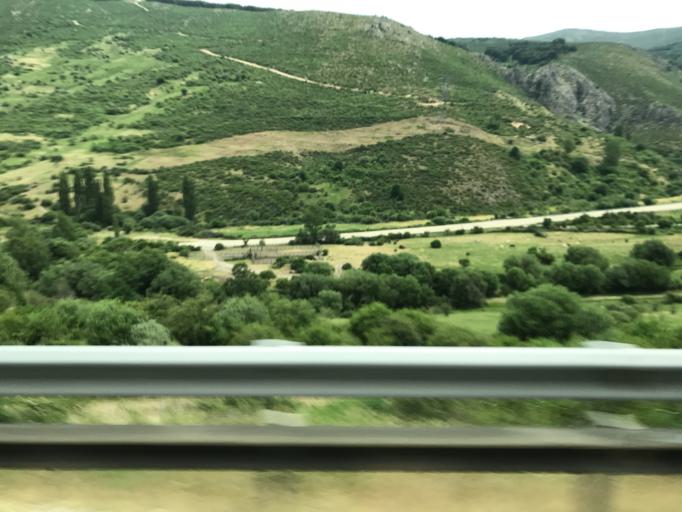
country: ES
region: Madrid
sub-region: Provincia de Madrid
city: Somosierra
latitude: 41.1462
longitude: -3.5830
